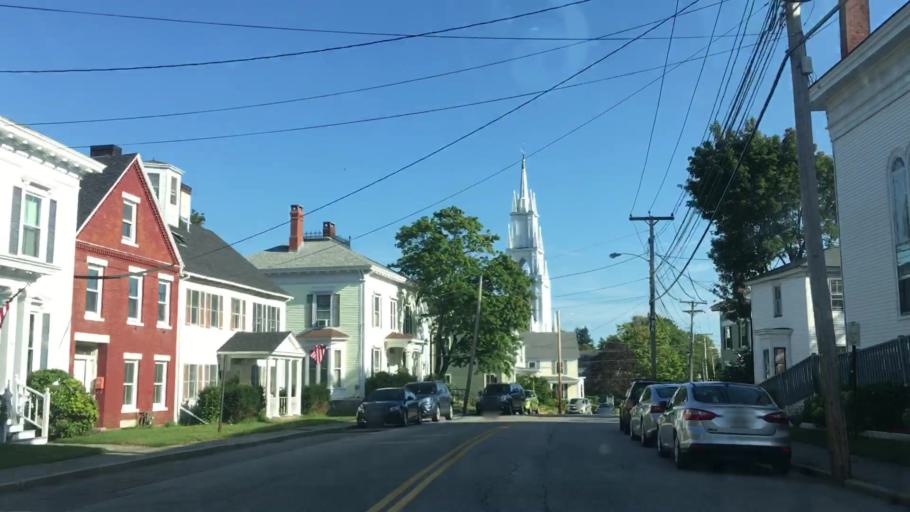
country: US
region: Maine
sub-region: Sagadahoc County
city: Bath
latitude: 43.9144
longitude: -69.8165
